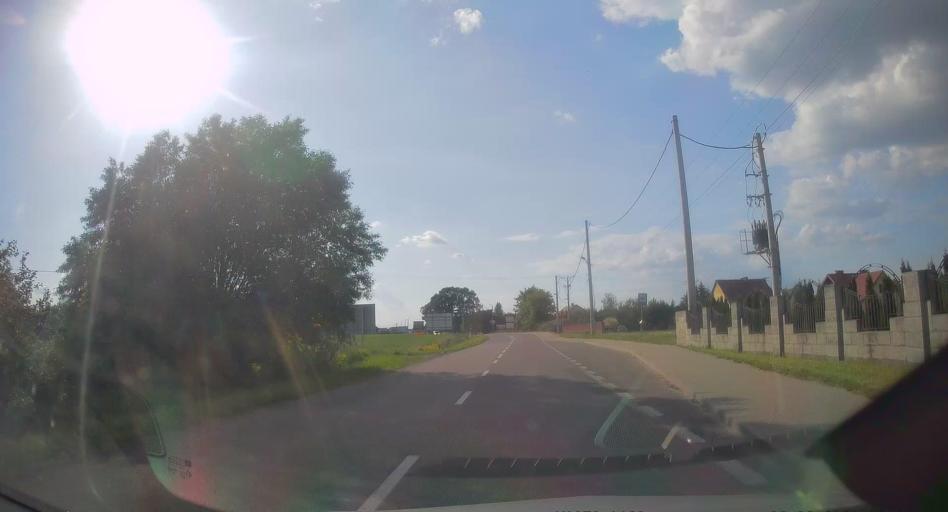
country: PL
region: Subcarpathian Voivodeship
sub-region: Powiat debicki
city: Zyrakow
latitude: 50.0705
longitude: 21.3974
